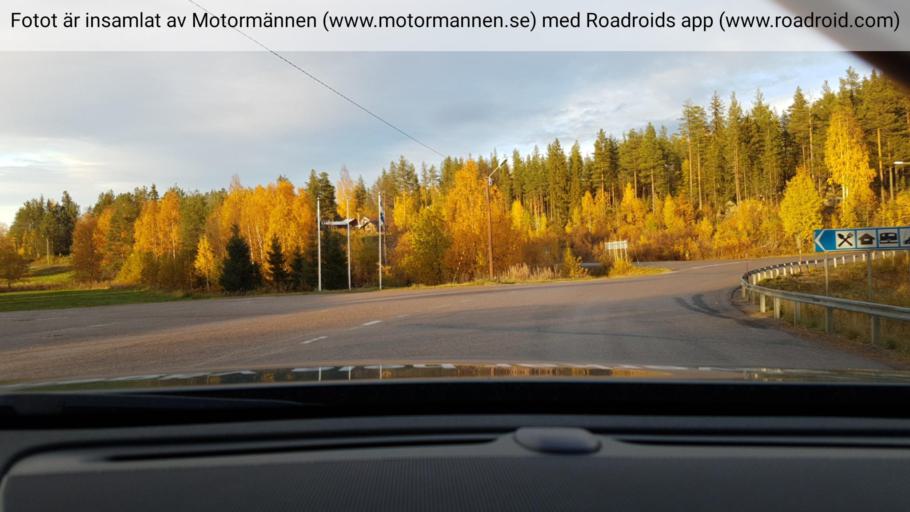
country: SE
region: Norrbotten
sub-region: Overkalix Kommun
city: OEverkalix
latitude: 66.6517
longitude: 22.7133
